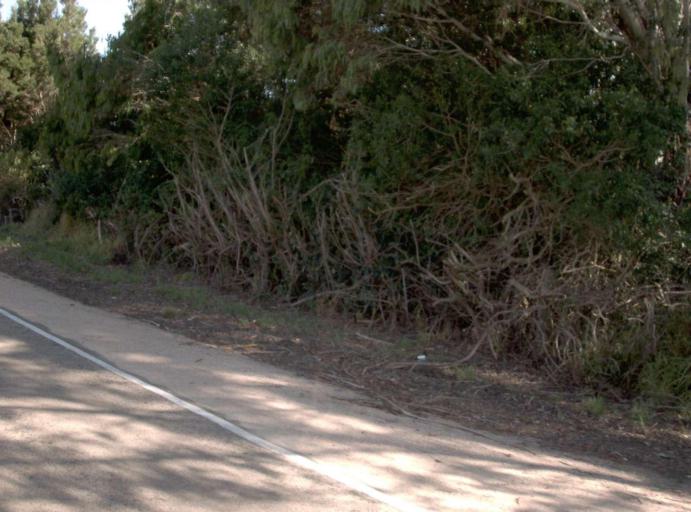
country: AU
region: Victoria
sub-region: East Gippsland
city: Lakes Entrance
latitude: -37.7209
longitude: 148.4769
